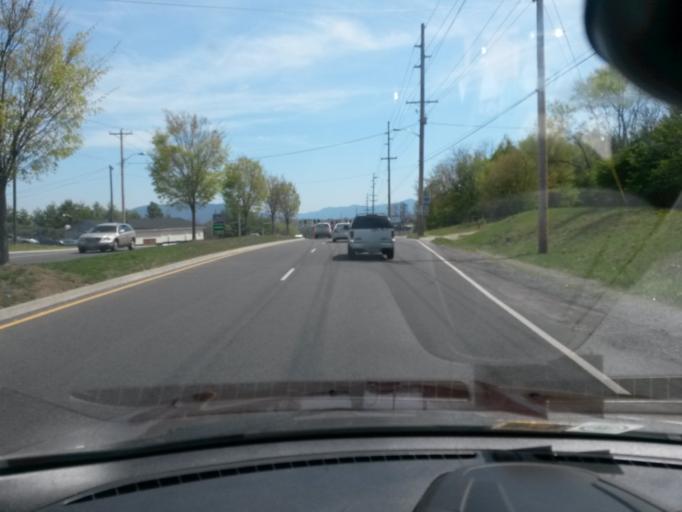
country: US
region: Virginia
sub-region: City of Roanoke
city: Roanoke
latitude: 37.3031
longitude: -79.9852
